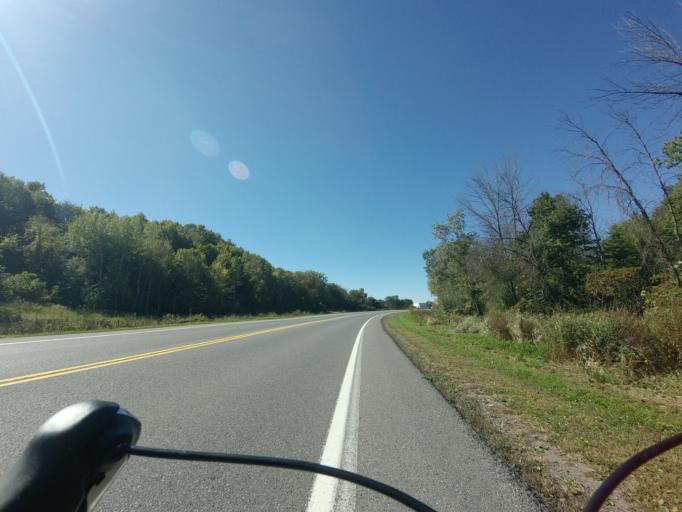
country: CA
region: Quebec
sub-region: Outaouais
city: Gatineau
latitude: 45.4594
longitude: -75.6286
